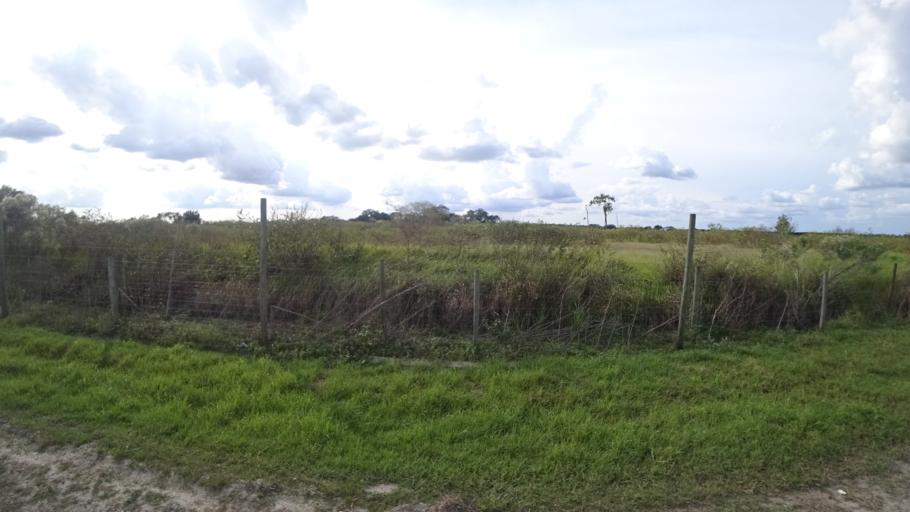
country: US
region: Florida
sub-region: DeSoto County
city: Nocatee
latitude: 27.2880
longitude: -82.1053
